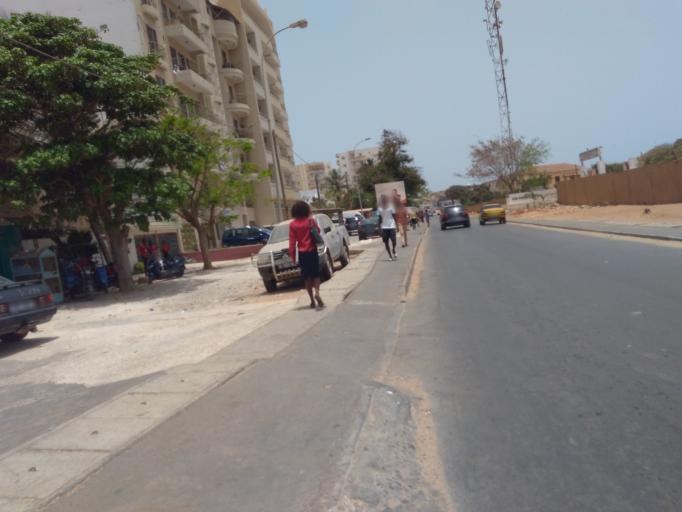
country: SN
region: Dakar
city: Grand Dakar
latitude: 14.7309
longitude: -17.4676
